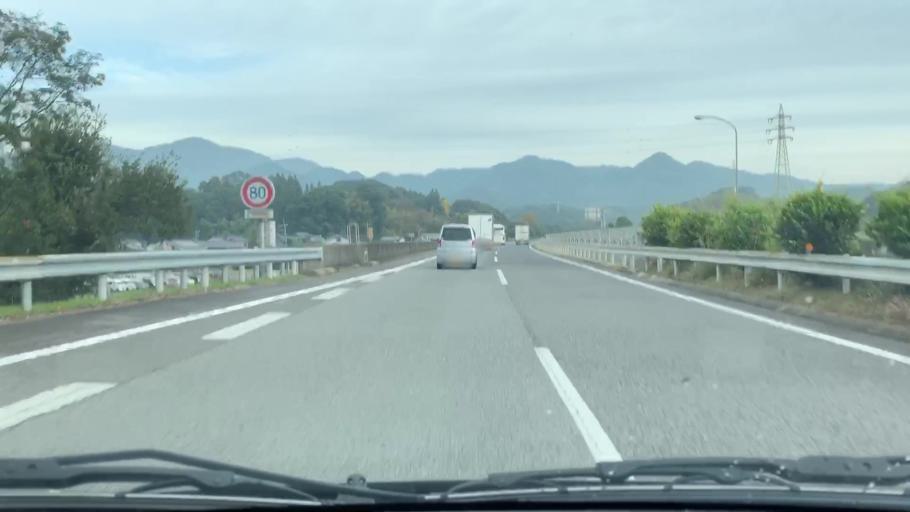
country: JP
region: Saga Prefecture
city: Takeocho-takeo
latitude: 33.2217
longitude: 130.0496
